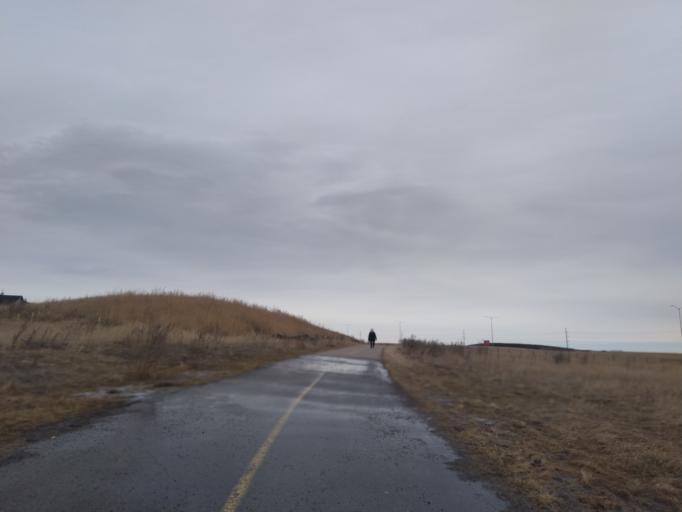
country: CA
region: Alberta
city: Chestermere
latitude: 51.1139
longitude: -113.9237
